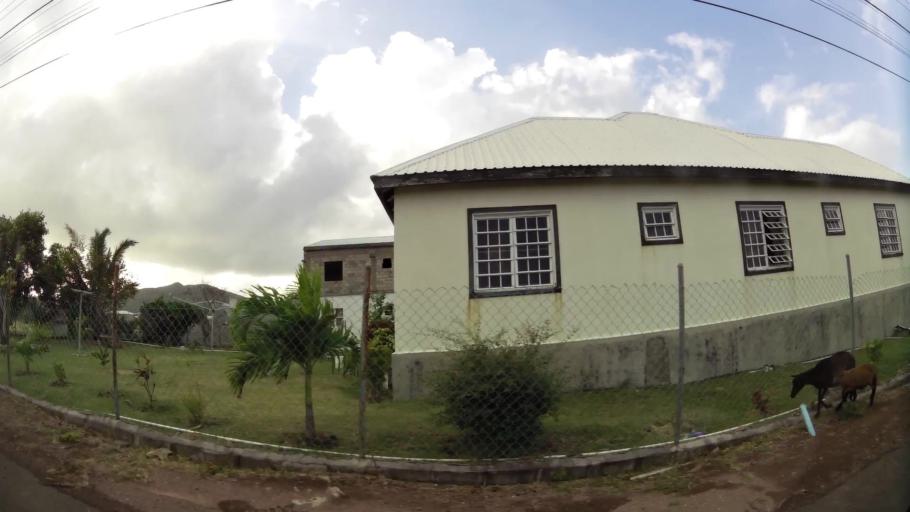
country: KN
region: Saint James Windwa
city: Newcastle
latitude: 17.1978
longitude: -62.5803
